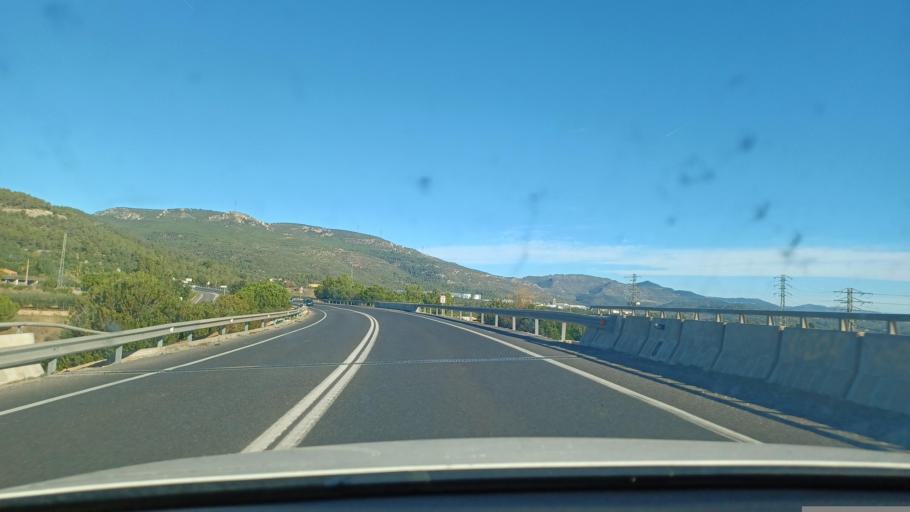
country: ES
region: Catalonia
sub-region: Provincia de Tarragona
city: Alcover
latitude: 41.2625
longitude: 1.1769
